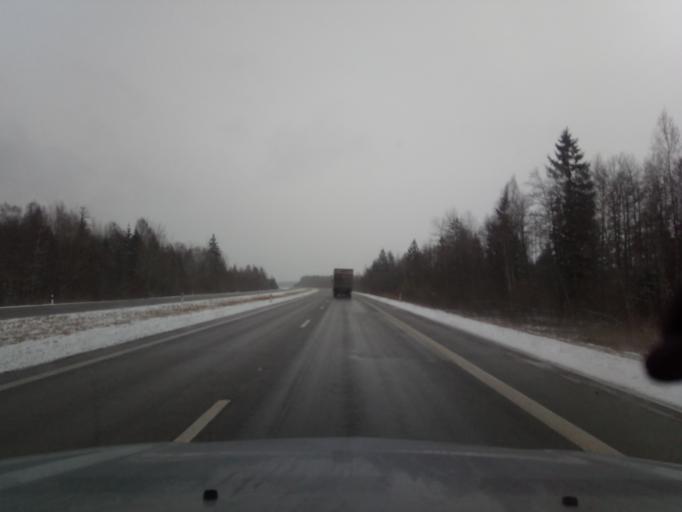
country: LT
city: Ramygala
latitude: 55.5345
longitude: 24.5466
